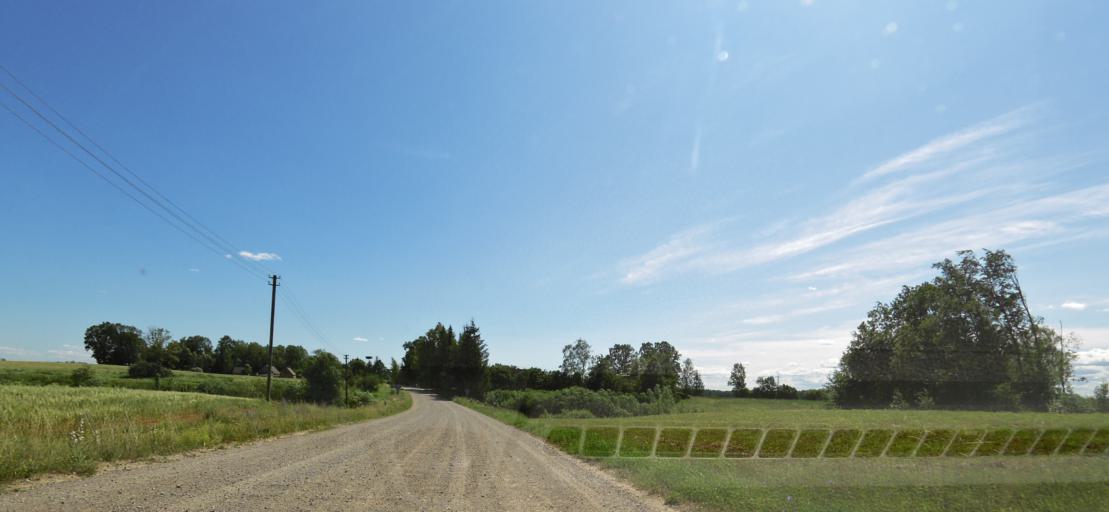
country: LT
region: Panevezys
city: Pasvalys
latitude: 56.2558
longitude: 24.3597
